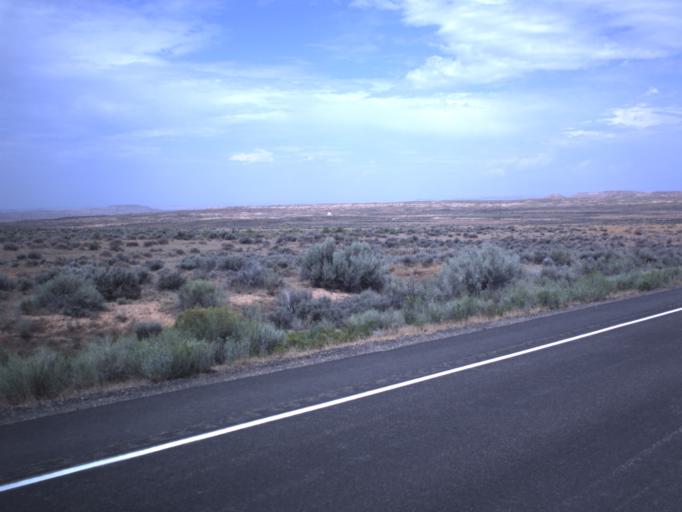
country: US
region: Utah
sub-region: Uintah County
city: Naples
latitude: 40.2403
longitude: -109.4156
